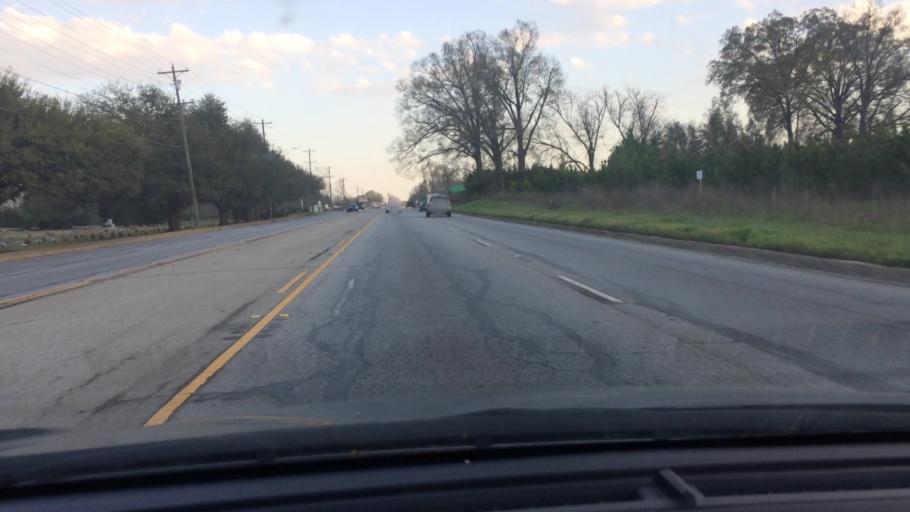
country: US
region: South Carolina
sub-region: Newberry County
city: Newberry
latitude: 34.2640
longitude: -81.5843
